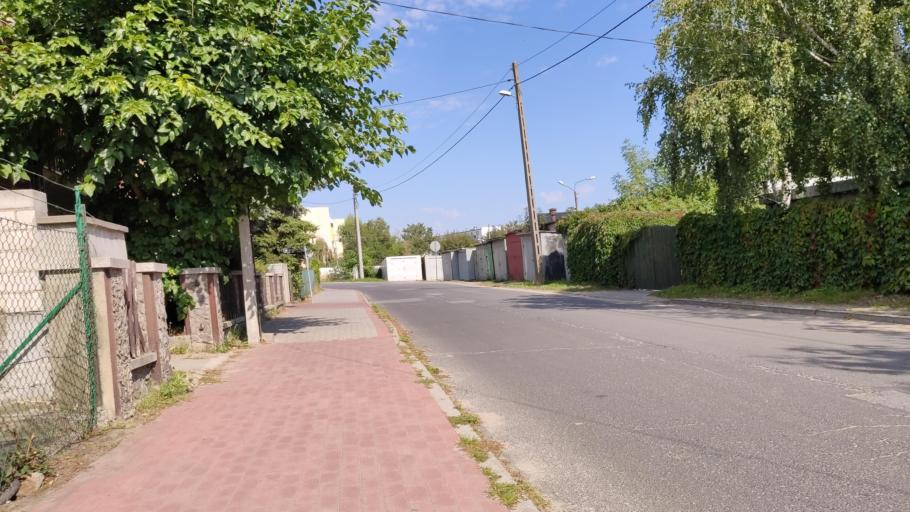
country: PL
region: Kujawsko-Pomorskie
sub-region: Powiat zninski
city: Znin
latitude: 52.8484
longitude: 17.7158
